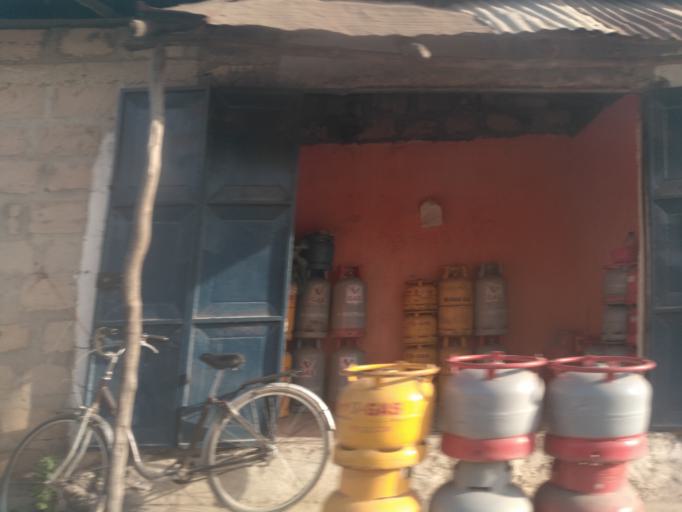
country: TZ
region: Zanzibar Urban/West
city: Zanzibar
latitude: -6.1753
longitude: 39.2079
